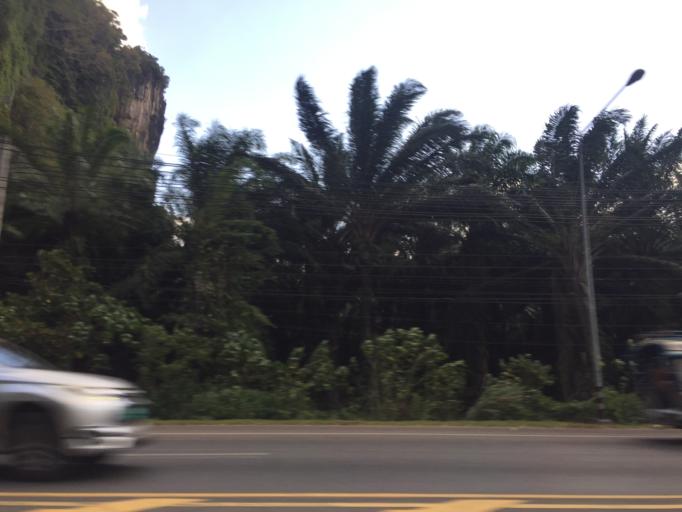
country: TH
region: Phangnga
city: Ban Ao Nang
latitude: 8.0745
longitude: 98.8417
